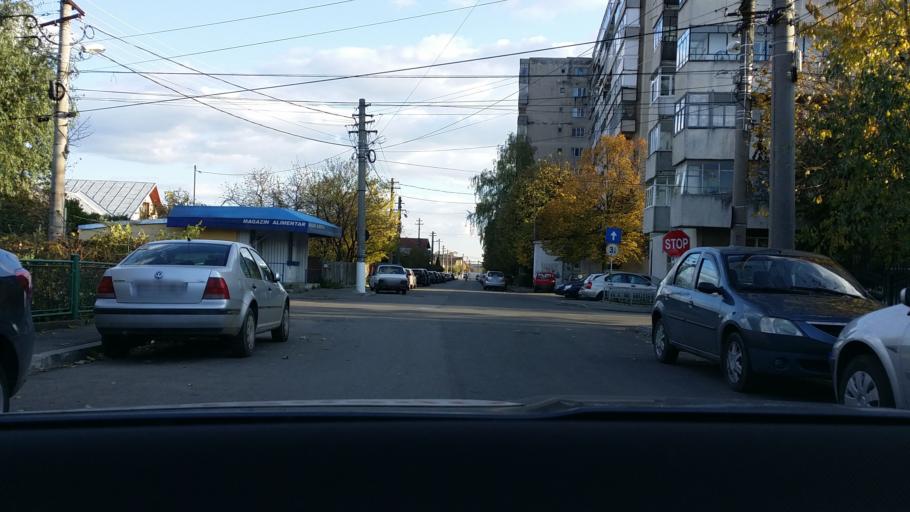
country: RO
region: Prahova
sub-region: Municipiul Campina
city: Campina
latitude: 45.1283
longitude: 25.7420
